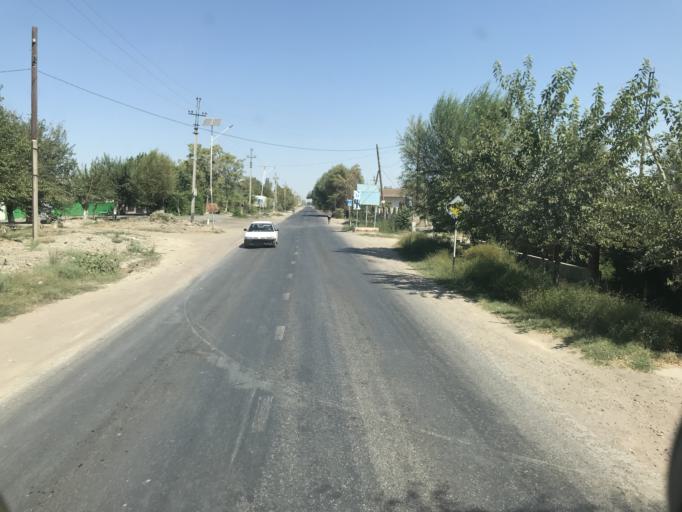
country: KZ
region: Ongtustik Qazaqstan
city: Ilyich
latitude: 40.9339
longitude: 68.4882
